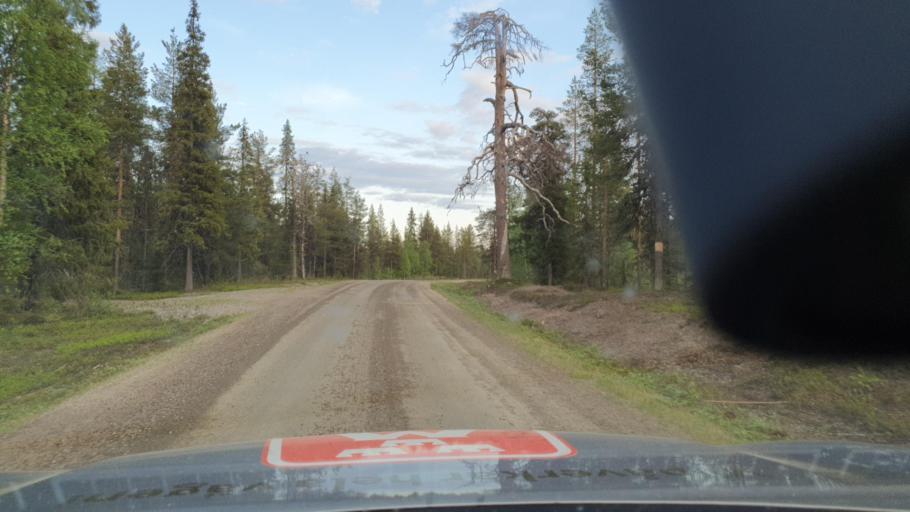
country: SE
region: Norrbotten
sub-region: Bodens Kommun
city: Boden
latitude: 66.5695
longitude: 21.4280
